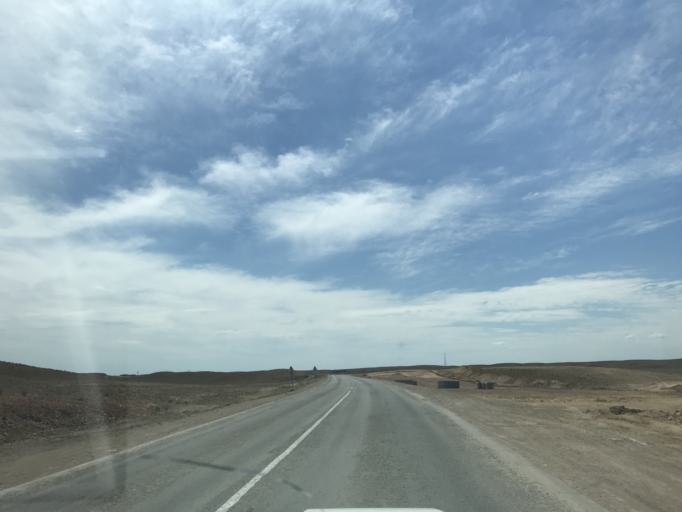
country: KZ
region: Almaty Oblysy
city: Ulken
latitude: 45.0815
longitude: 73.9714
